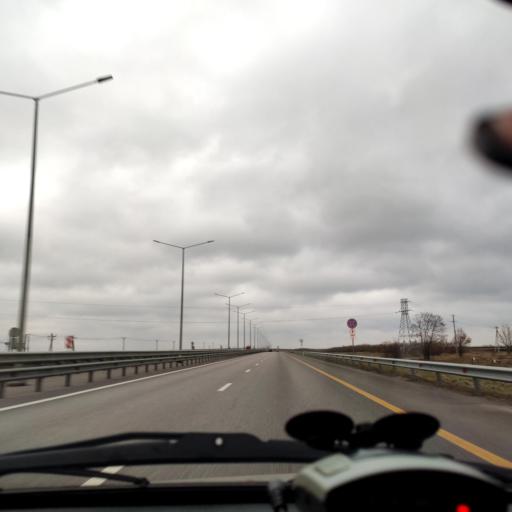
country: RU
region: Voronezj
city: Novaya Usman'
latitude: 51.5975
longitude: 39.3524
